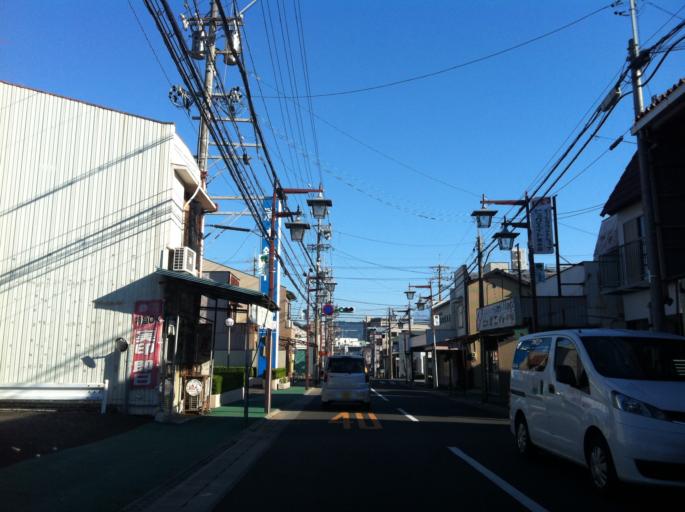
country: JP
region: Shizuoka
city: Shizuoka-shi
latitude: 35.0176
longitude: 138.4805
